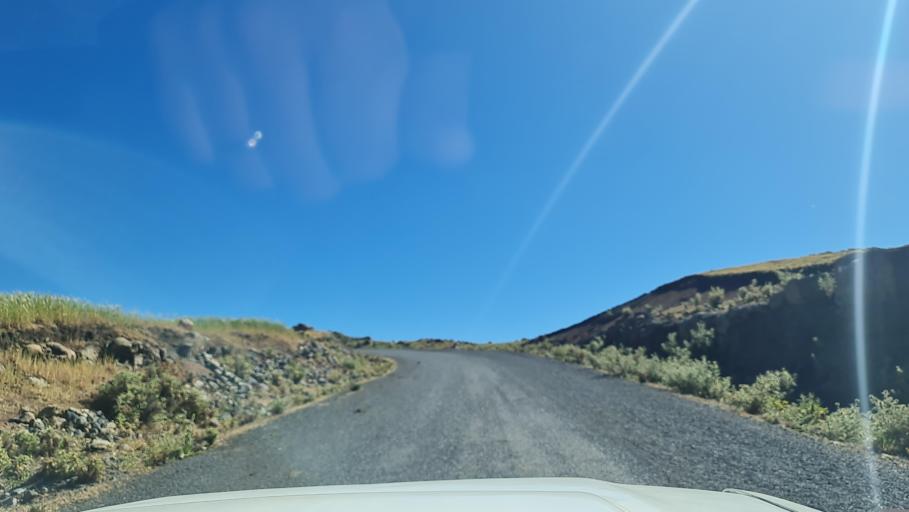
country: ET
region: Amhara
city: Debark'
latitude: 13.1344
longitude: 38.1748
